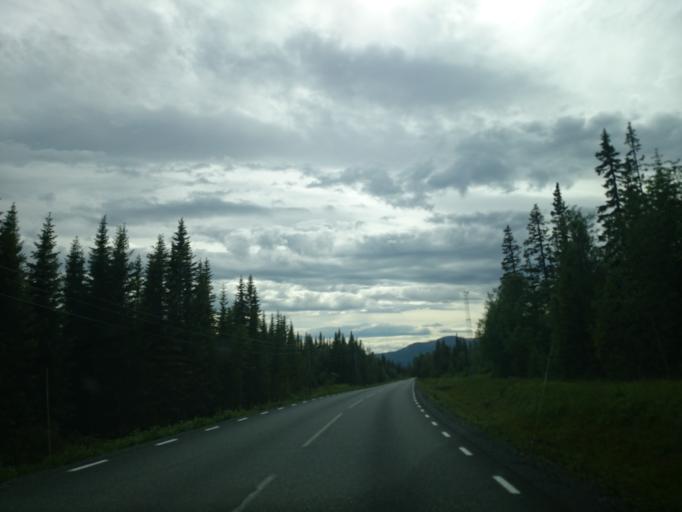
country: SE
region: Jaemtland
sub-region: Are Kommun
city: Are
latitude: 63.2485
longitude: 13.1986
